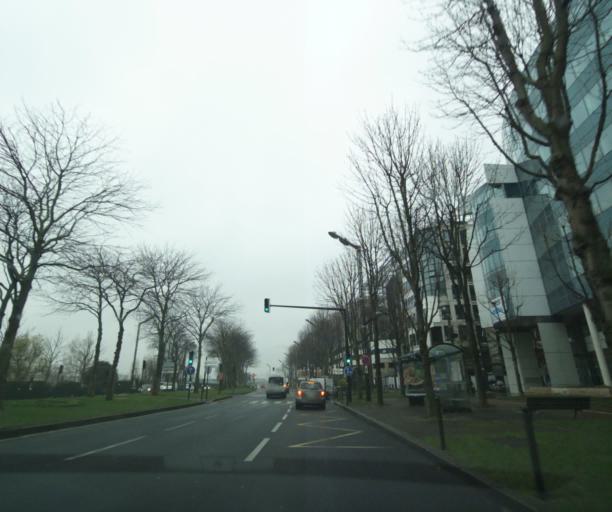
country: FR
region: Ile-de-France
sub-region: Departement des Hauts-de-Seine
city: Levallois-Perret
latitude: 48.9006
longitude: 2.2838
